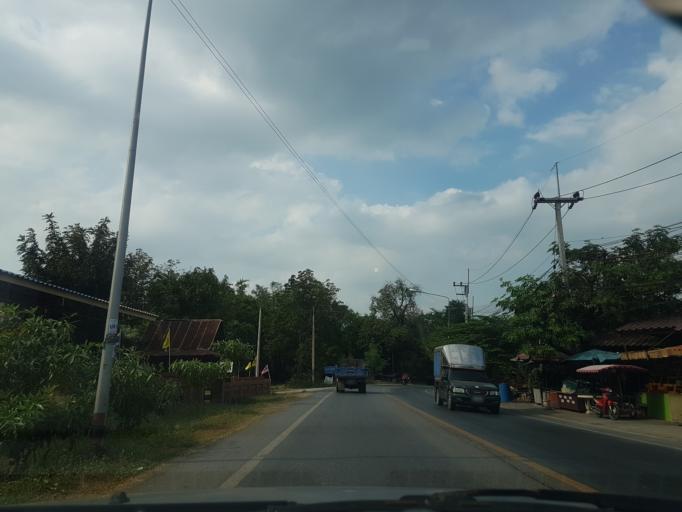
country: TH
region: Phra Nakhon Si Ayutthaya
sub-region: Amphoe Tha Ruea
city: Tha Ruea
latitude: 14.5583
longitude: 100.7201
